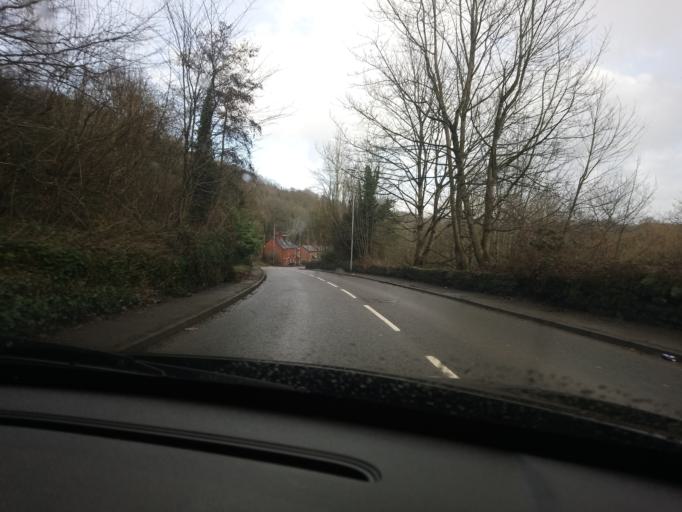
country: GB
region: Wales
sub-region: Wrexham
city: Chirk
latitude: 52.9669
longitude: -3.0639
